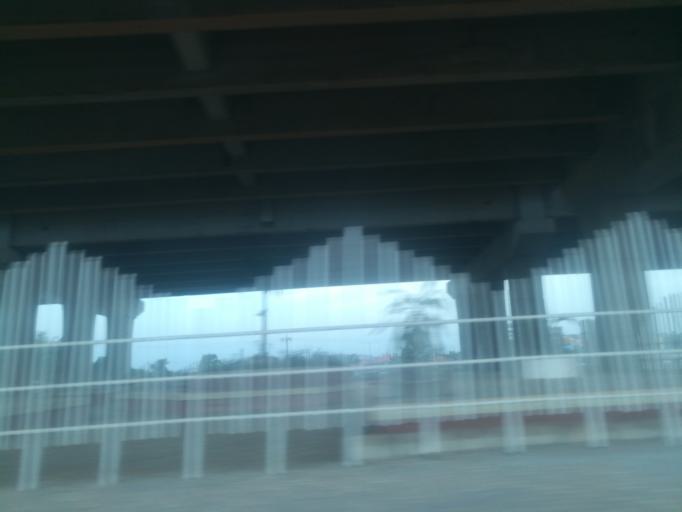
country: NG
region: Ogun
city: Abeokuta
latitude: 7.1262
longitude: 3.3570
